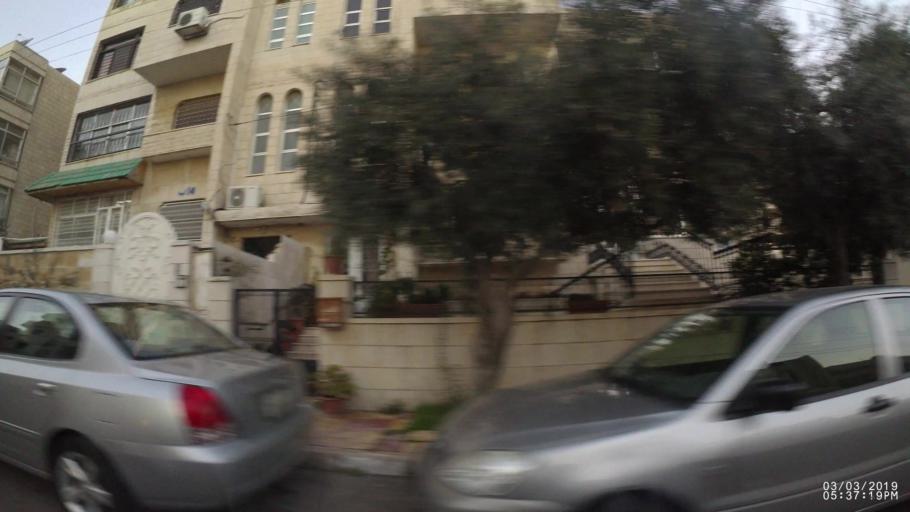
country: JO
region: Amman
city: Al Jubayhah
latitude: 31.9912
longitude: 35.8837
